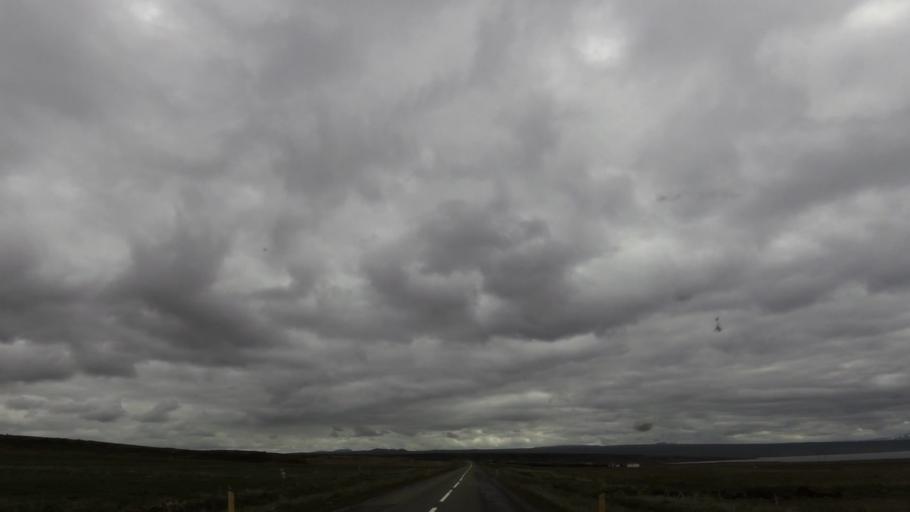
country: IS
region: West
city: Borgarnes
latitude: 65.2248
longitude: -21.7549
